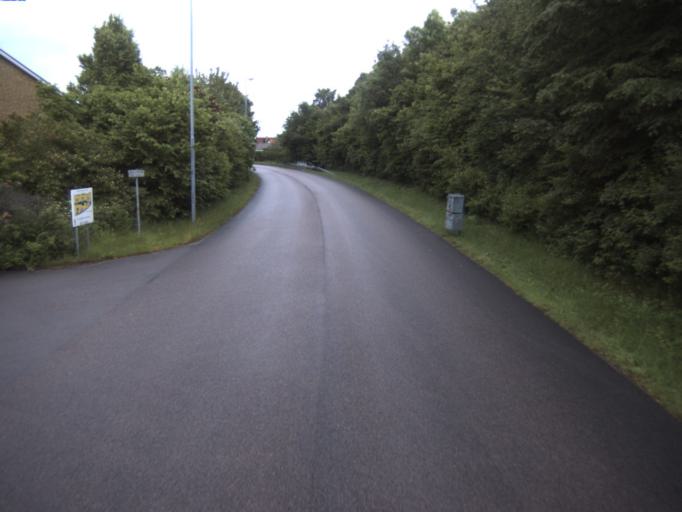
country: SE
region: Skane
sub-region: Helsingborg
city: Rydeback
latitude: 56.0169
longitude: 12.7492
